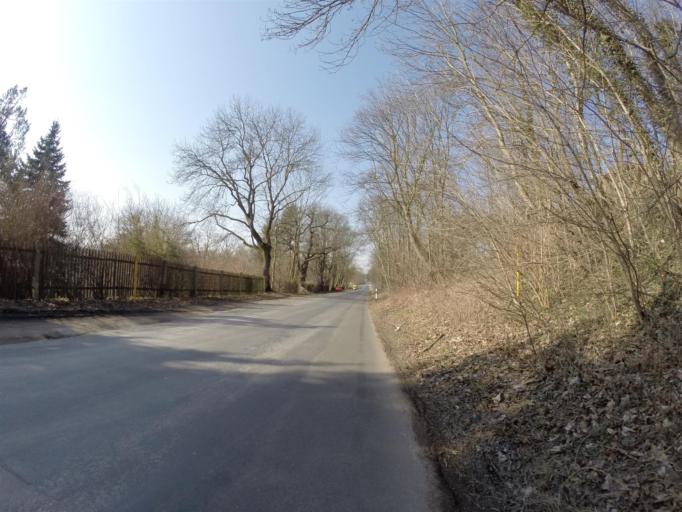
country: DE
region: Thuringia
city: Weimar
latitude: 50.9596
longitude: 11.3552
